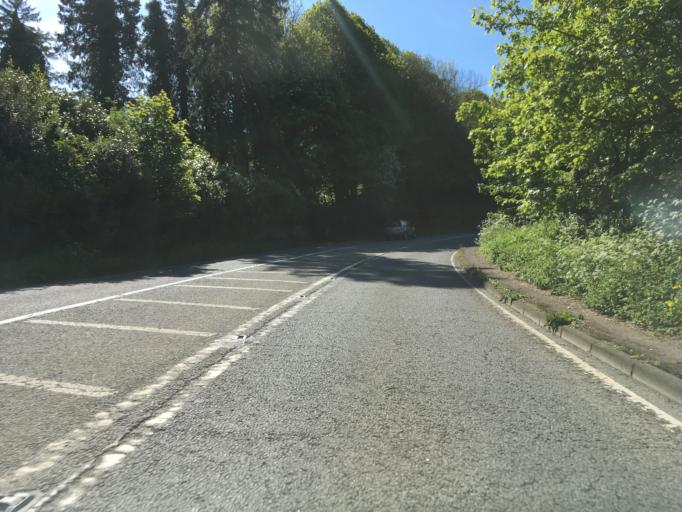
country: GB
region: England
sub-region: Gloucestershire
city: Nailsworth
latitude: 51.6808
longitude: -2.2220
